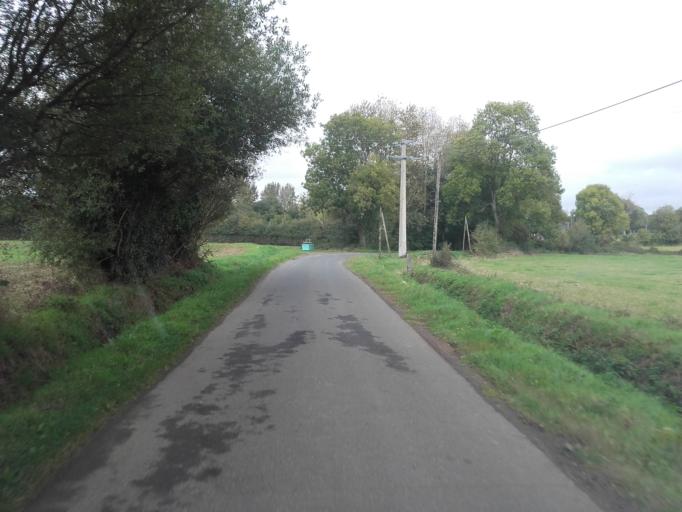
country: FR
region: Brittany
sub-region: Departement des Cotes-d'Armor
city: Pleguien
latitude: 48.6177
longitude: -2.9359
